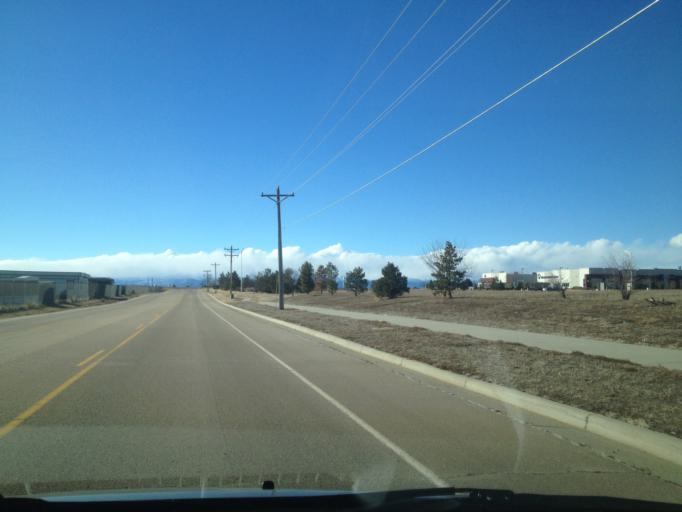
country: US
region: Colorado
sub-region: Weld County
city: Dacono
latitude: 40.0731
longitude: -104.9759
